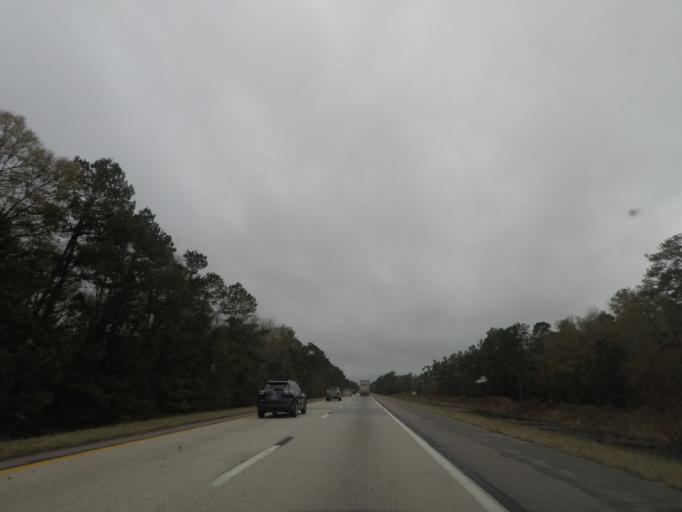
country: US
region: South Carolina
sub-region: Dorchester County
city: Saint George
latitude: 33.1146
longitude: -80.6431
